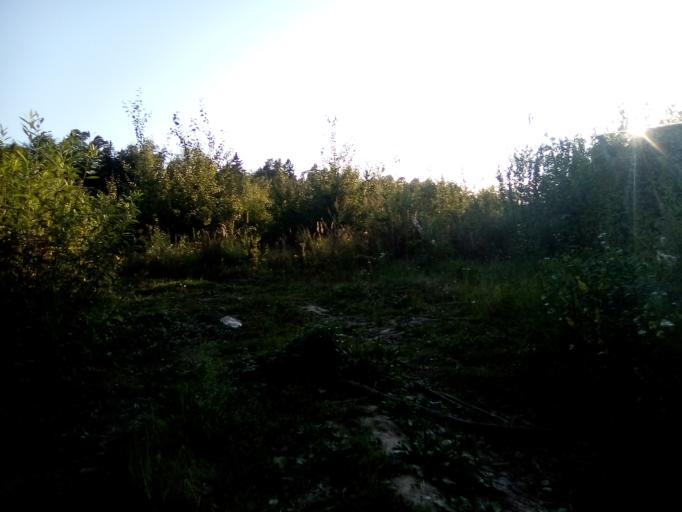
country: RU
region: Moskovskaya
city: Krasnoznamensk
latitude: 55.5816
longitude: 37.0502
